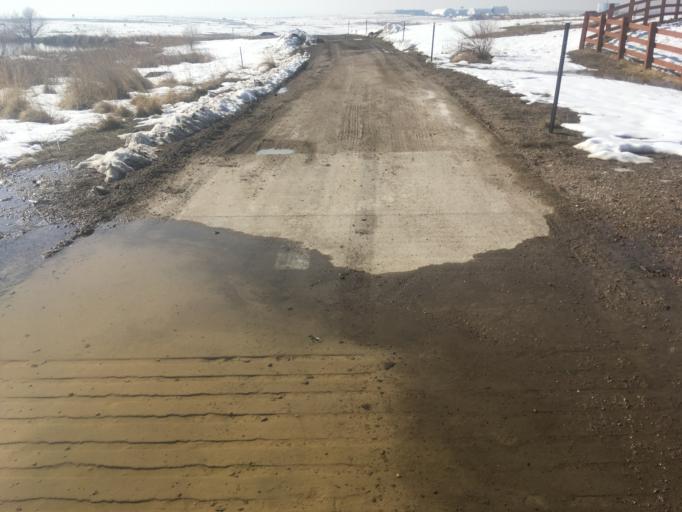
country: US
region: Colorado
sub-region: Boulder County
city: Lafayette
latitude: 39.9727
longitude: -105.0552
